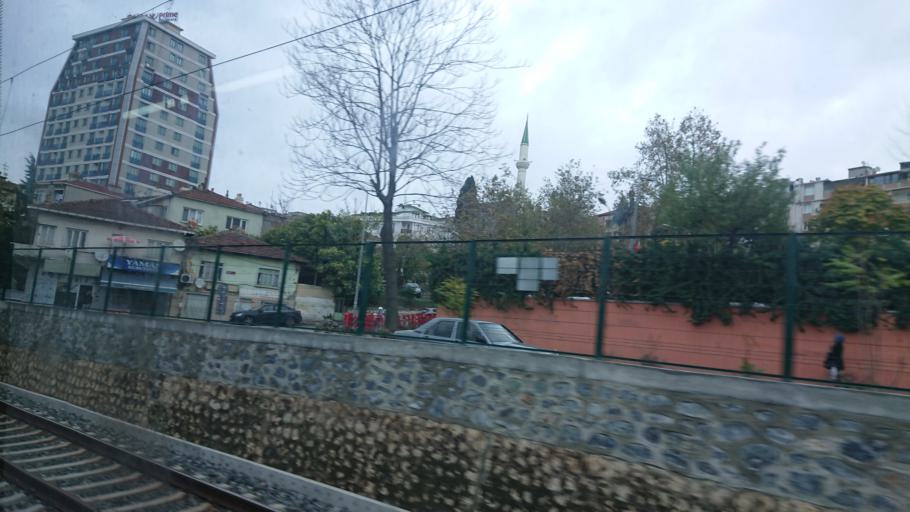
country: TR
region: Istanbul
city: Mahmutbey
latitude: 40.9912
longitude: 28.7720
